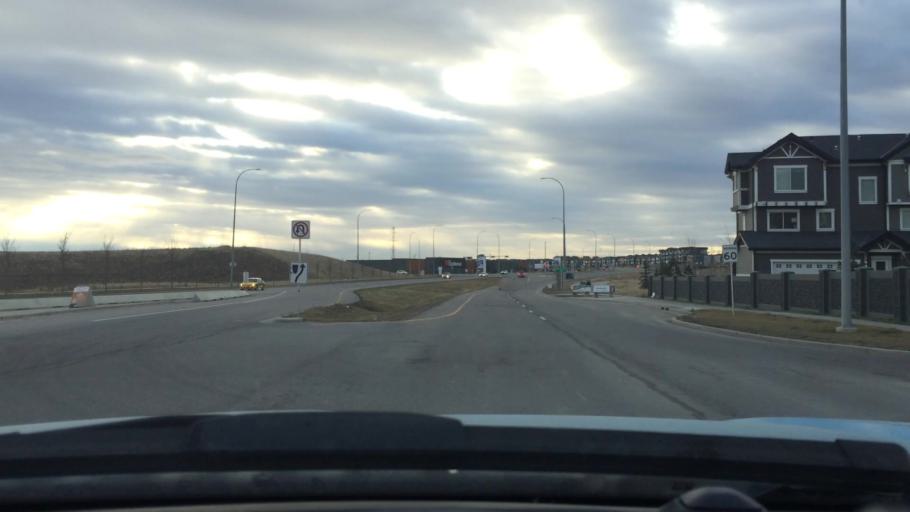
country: CA
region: Alberta
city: Calgary
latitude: 51.1728
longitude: -114.1550
